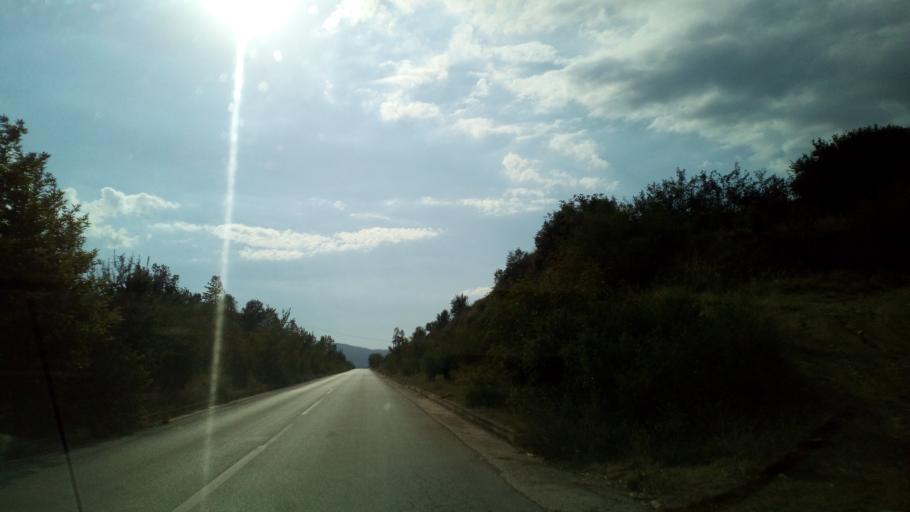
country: GR
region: Central Macedonia
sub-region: Nomos Thessalonikis
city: Gerakarou
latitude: 40.5898
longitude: 23.2507
